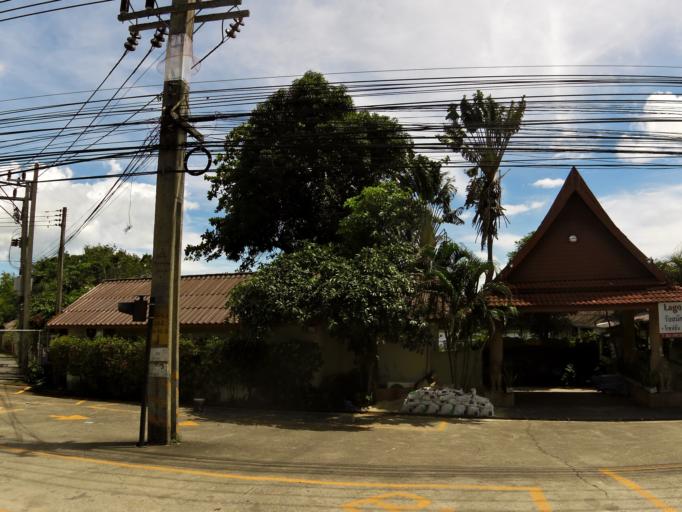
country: TH
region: Phuket
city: Mueang Phuket
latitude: 7.8669
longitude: 98.3544
